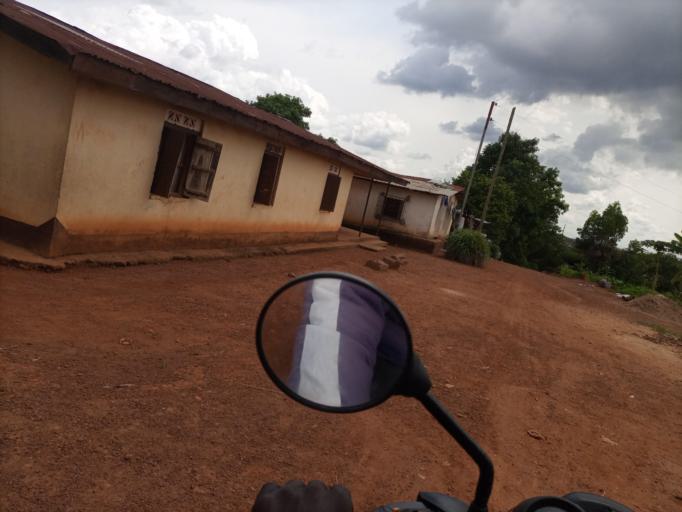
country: SL
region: Southern Province
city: Bo
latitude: 7.9502
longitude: -11.7407
